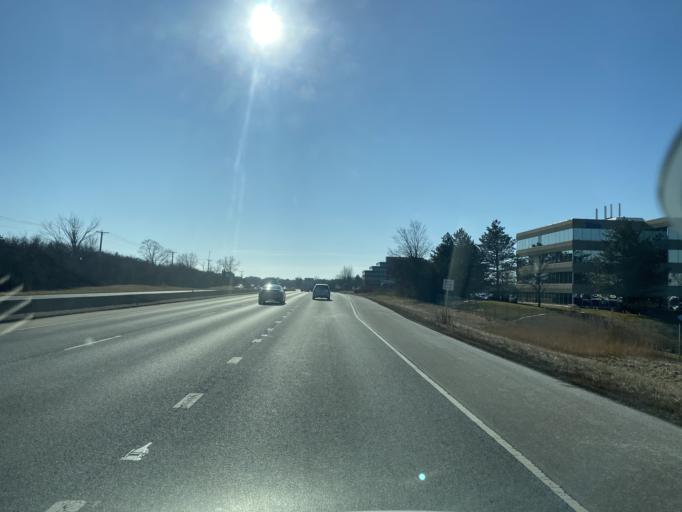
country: US
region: Illinois
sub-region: DuPage County
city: Clarendon Hills
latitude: 41.8220
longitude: -87.9534
